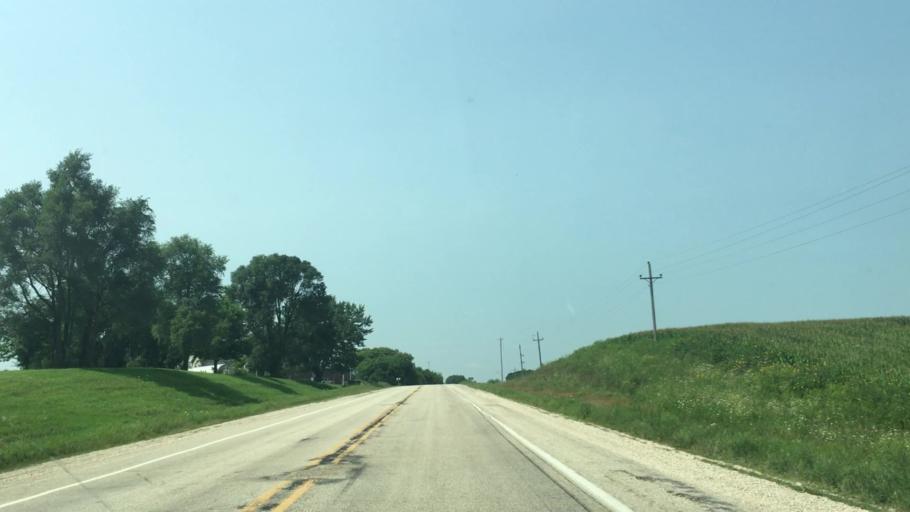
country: US
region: Iowa
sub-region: Fayette County
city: West Union
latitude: 43.0806
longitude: -91.8425
